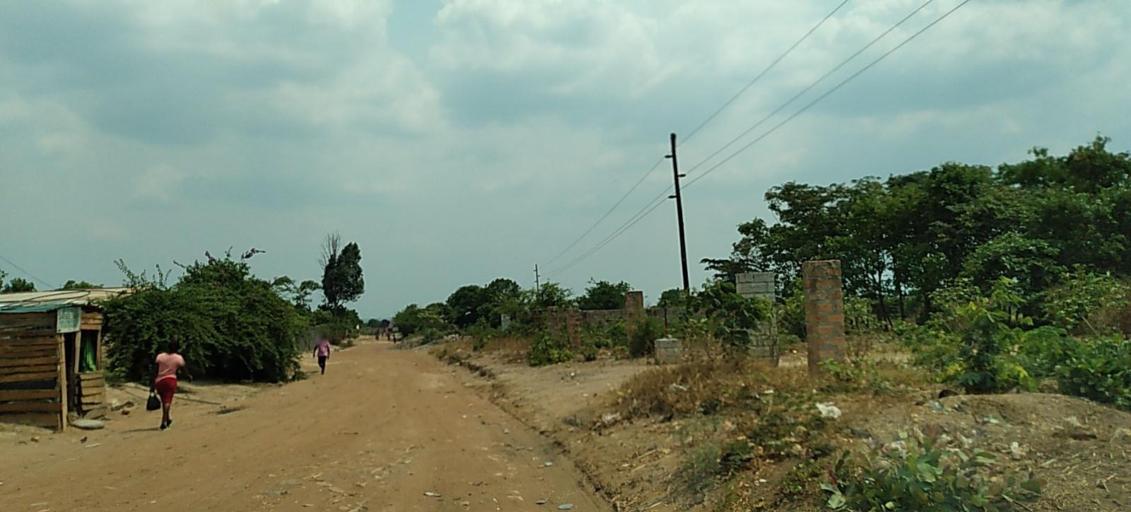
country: ZM
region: Copperbelt
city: Kalulushi
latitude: -12.8538
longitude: 28.0784
